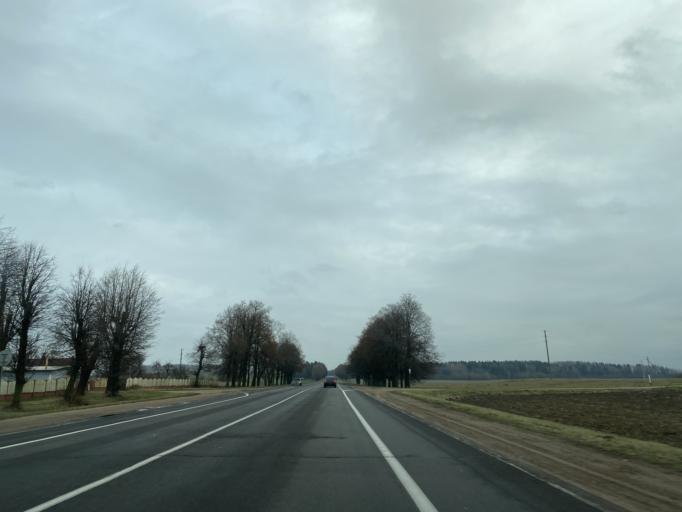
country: BY
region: Minsk
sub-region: Smalyavitski Rayon
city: Oktjabr'skij
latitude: 54.0724
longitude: 28.1942
